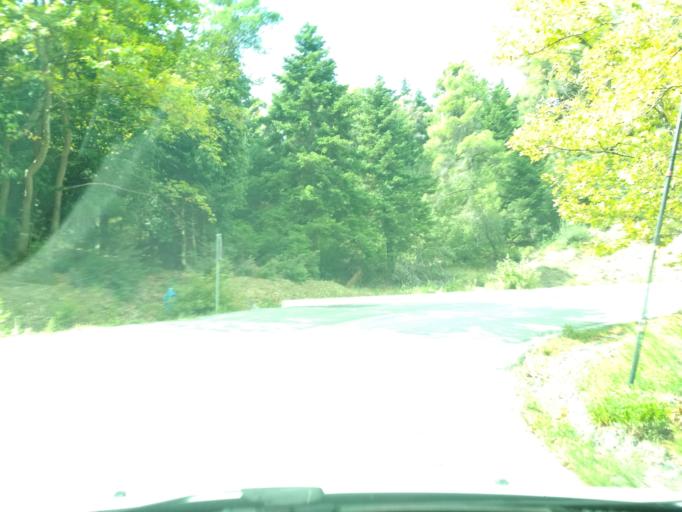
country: GR
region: Central Greece
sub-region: Nomos Evvoias
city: Politika
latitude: 38.6594
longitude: 23.5579
